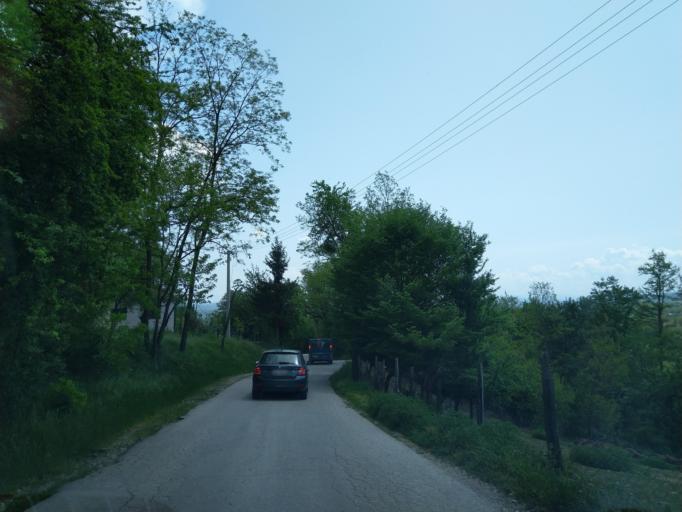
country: RS
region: Central Serbia
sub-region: Zlatiborski Okrug
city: Pozega
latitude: 43.8638
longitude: 19.9443
